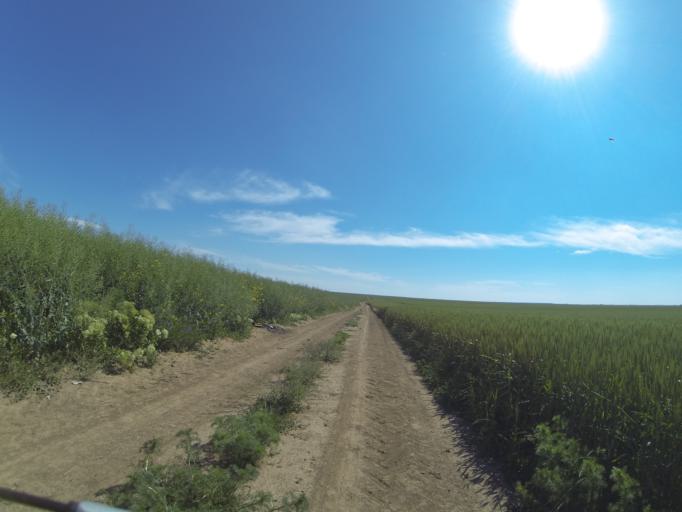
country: RO
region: Dolj
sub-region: Comuna Cosoveni
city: Cosoveni
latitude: 44.2581
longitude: 23.9992
